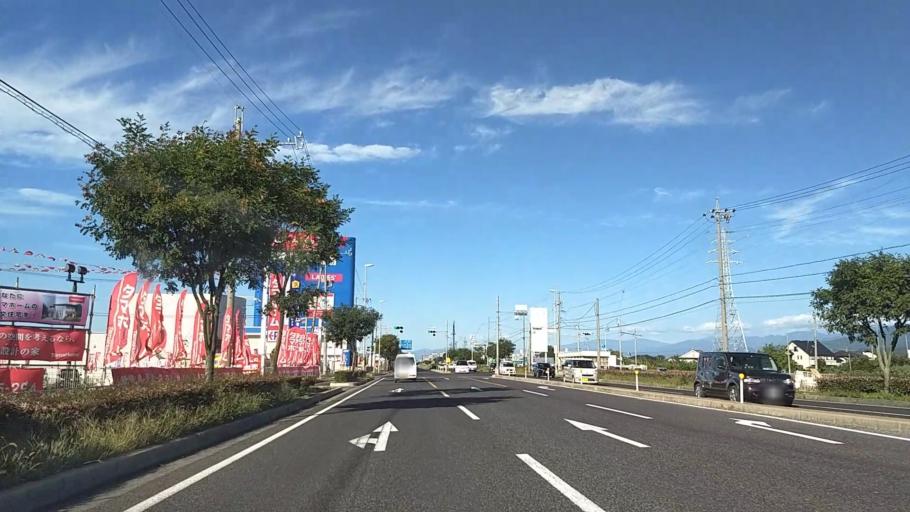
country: JP
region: Nagano
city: Nagano-shi
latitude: 36.5714
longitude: 138.1523
